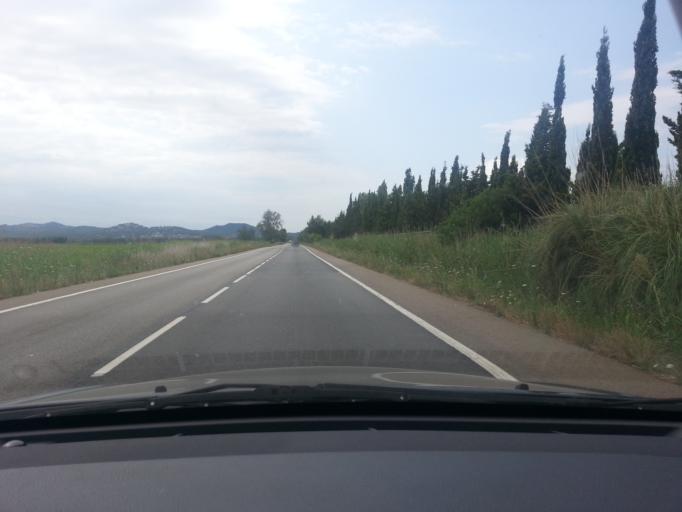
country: ES
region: Catalonia
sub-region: Provincia de Girona
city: Torroella de Montgri
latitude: 42.0146
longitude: 3.1430
